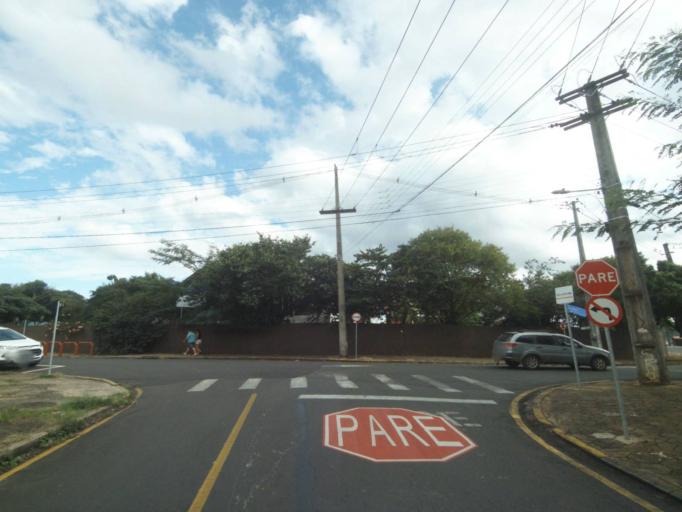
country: BR
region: Parana
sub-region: Telemaco Borba
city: Telemaco Borba
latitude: -24.3386
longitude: -50.6118
